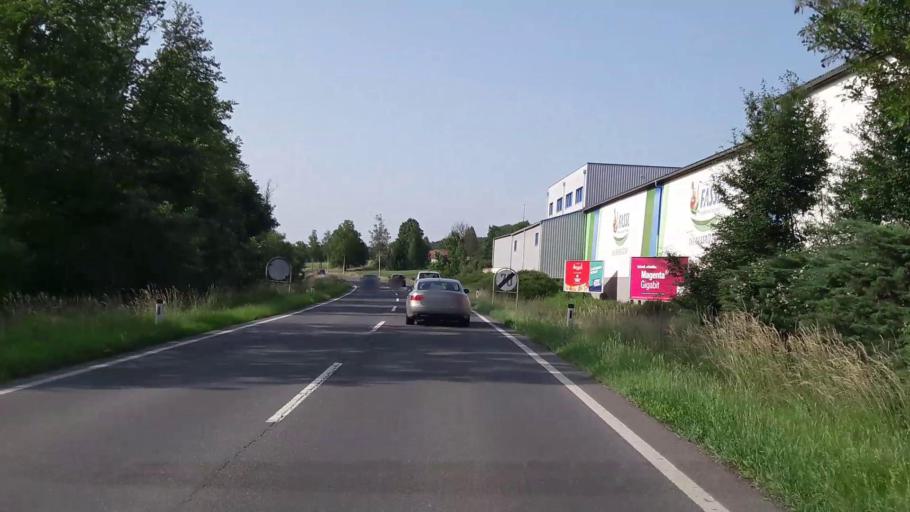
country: AT
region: Burgenland
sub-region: Politischer Bezirk Oberwart
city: Litzelsdorf
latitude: 47.2140
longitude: 16.1636
